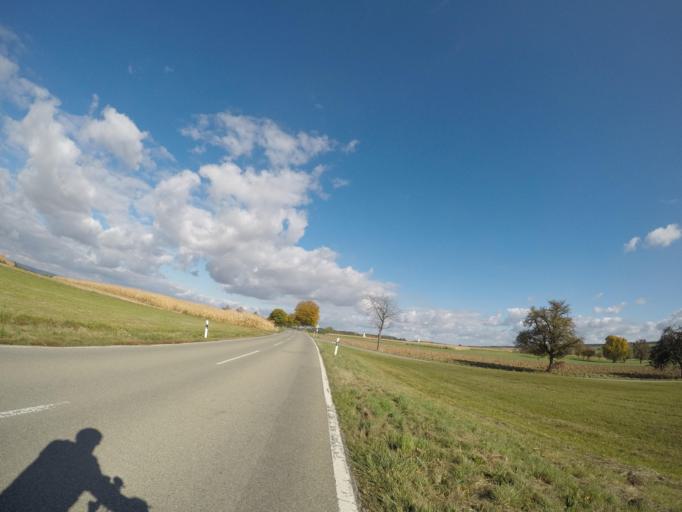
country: DE
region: Baden-Wuerttemberg
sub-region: Tuebingen Region
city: Grundsheim
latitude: 48.1625
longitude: 9.6789
